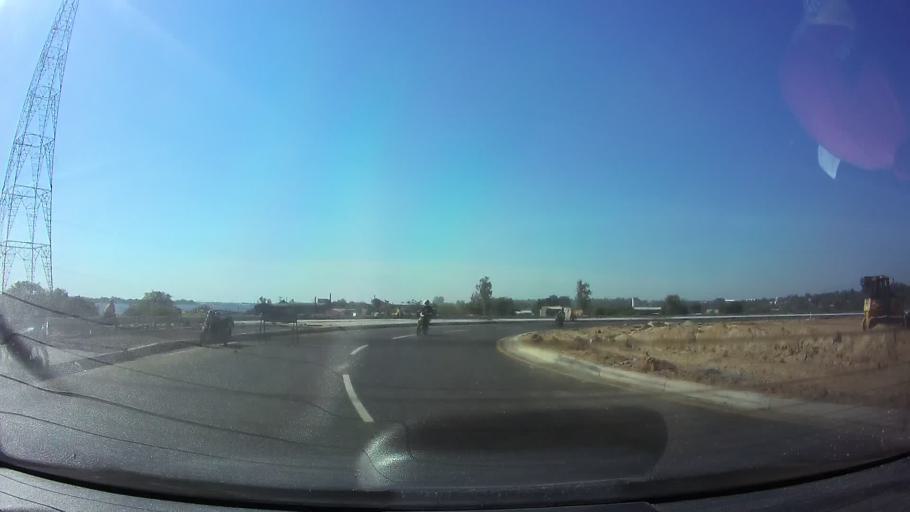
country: PY
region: Asuncion
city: Asuncion
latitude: -25.2446
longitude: -57.5907
